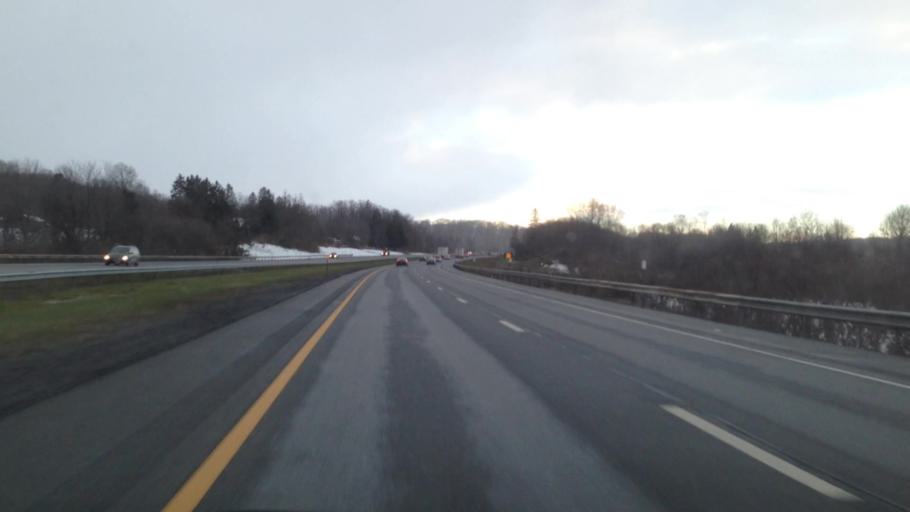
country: US
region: New York
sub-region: Herkimer County
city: Little Falls
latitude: 43.0070
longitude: -74.7804
